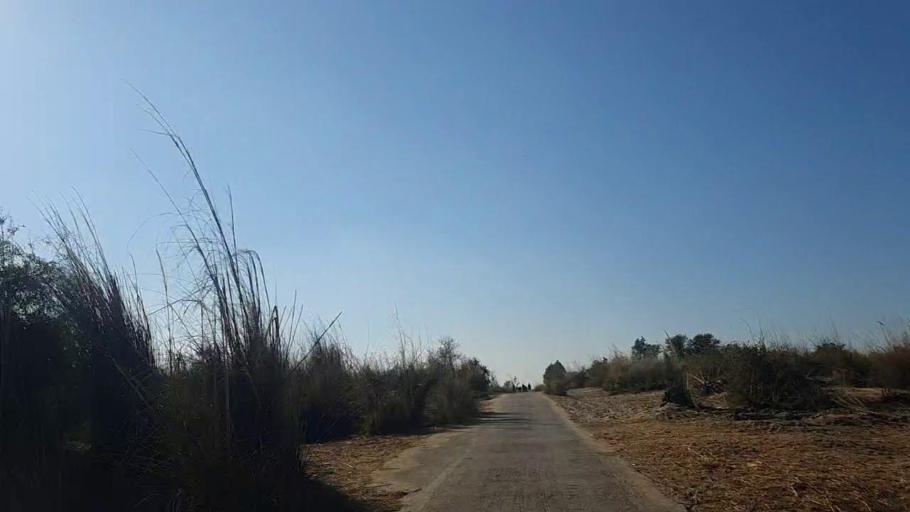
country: PK
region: Sindh
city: Sanghar
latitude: 26.2415
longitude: 68.8997
